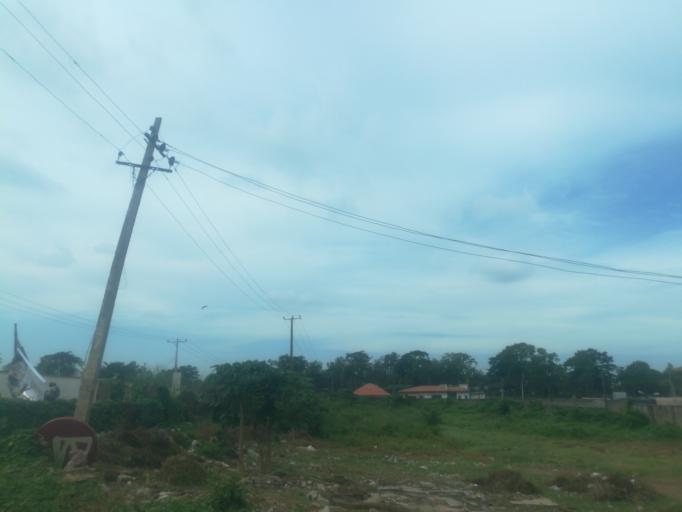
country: NG
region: Oyo
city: Ibadan
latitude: 7.3915
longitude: 3.9693
